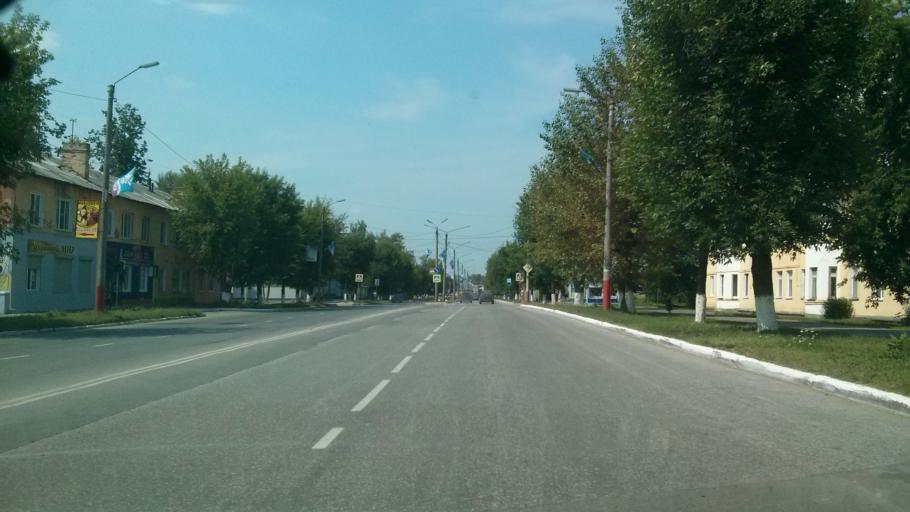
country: RU
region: Vladimir
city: Murom
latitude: 55.5687
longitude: 42.0406
